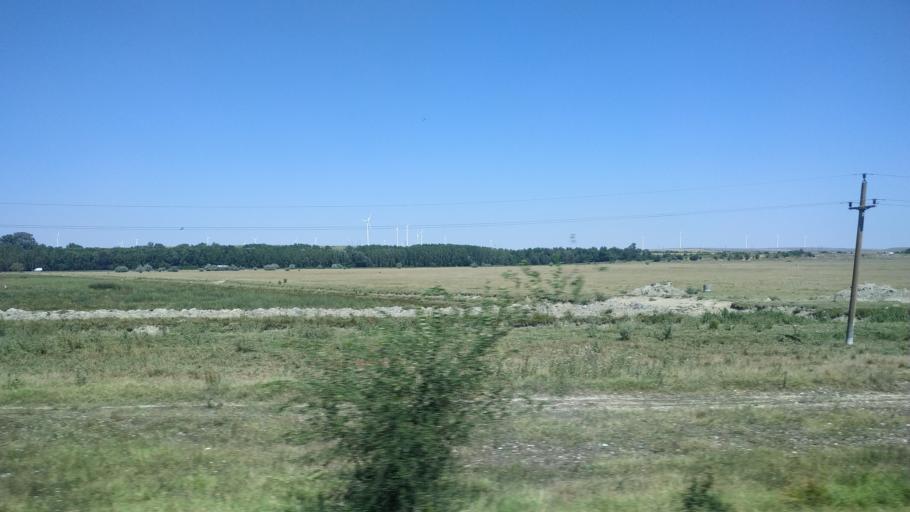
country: RO
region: Constanta
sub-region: Comuna Mircea Voda
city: Mircea Voda
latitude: 44.2645
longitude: 28.1615
